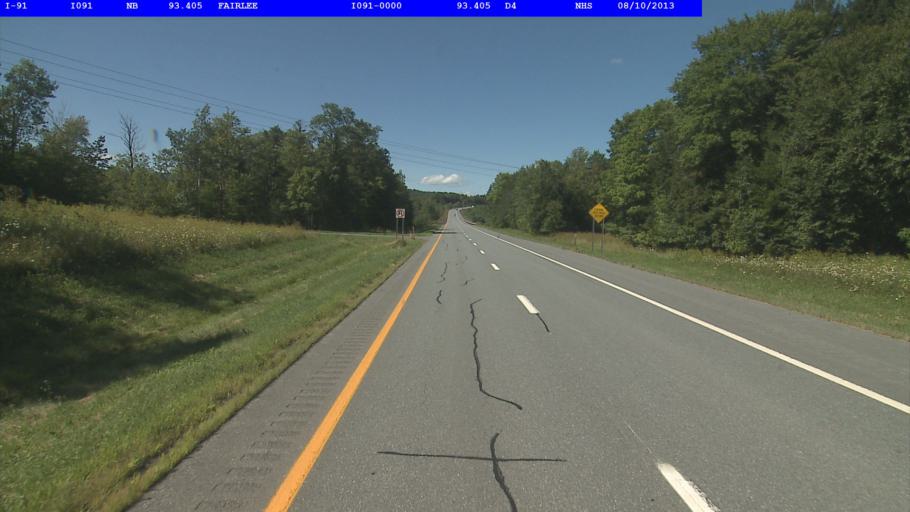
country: US
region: New Hampshire
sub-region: Grafton County
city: Orford
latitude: 43.9246
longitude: -72.1328
